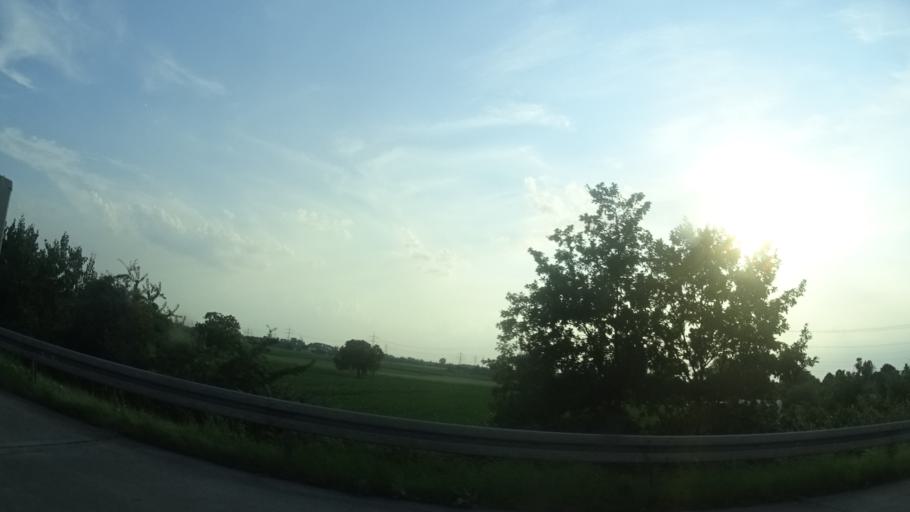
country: DE
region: Baden-Wuerttemberg
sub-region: Karlsruhe Region
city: Weinheim
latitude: 49.5396
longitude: 8.6298
